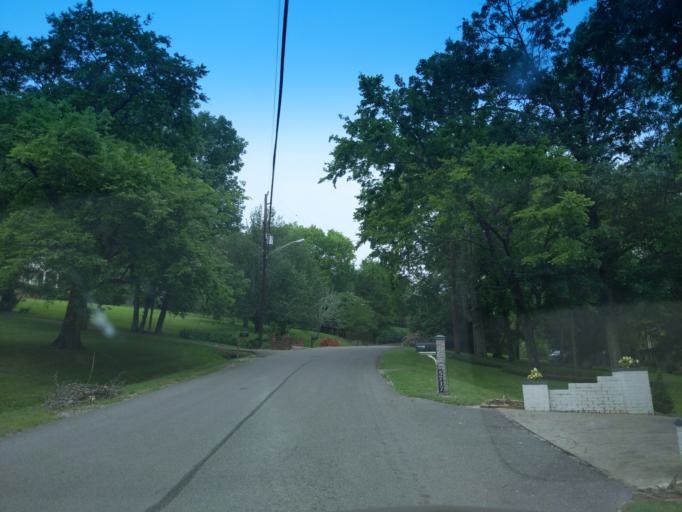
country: US
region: Tennessee
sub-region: Williamson County
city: Brentwood Estates
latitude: 36.0285
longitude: -86.7646
